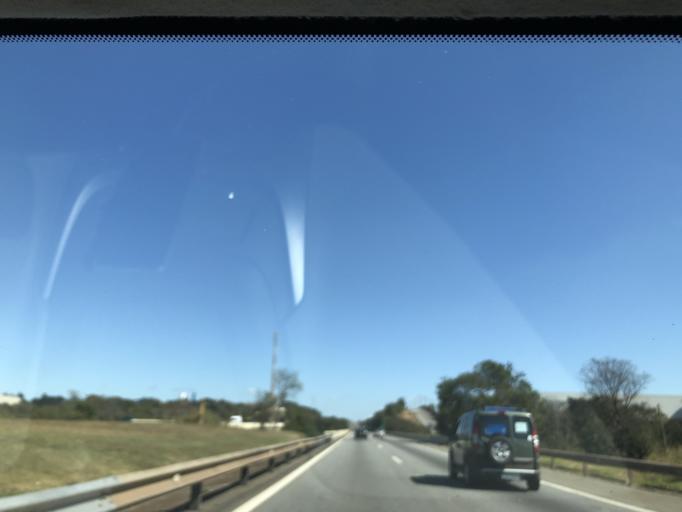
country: BR
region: Sao Paulo
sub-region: Sorocaba
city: Sorocaba
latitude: -23.4206
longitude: -47.3524
